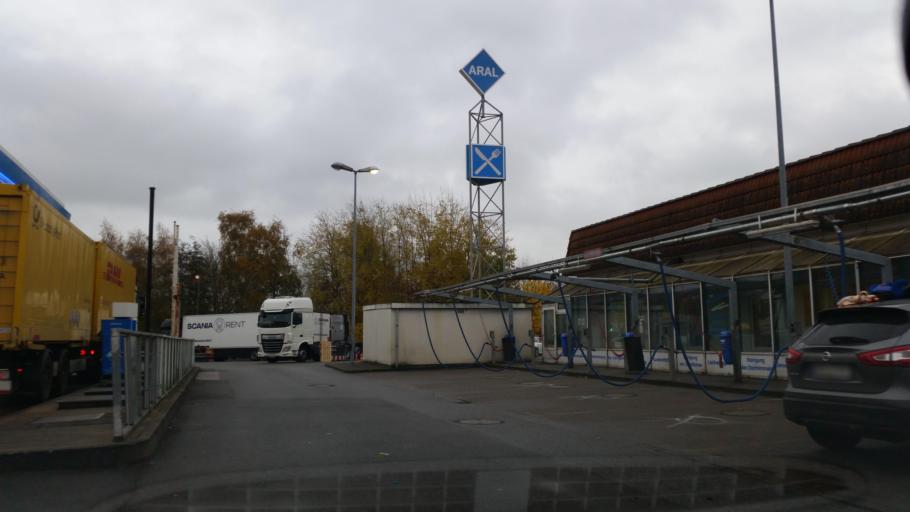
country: DE
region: Hamburg
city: Wandsbek
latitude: 53.4895
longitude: 10.1147
